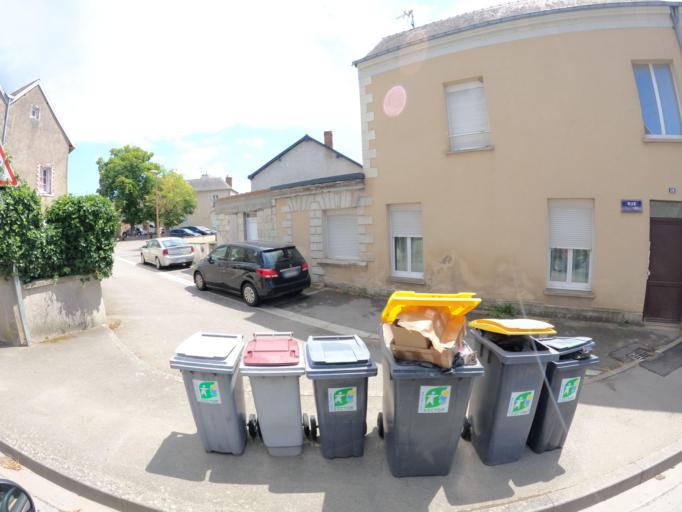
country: FR
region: Pays de la Loire
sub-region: Departement de Maine-et-Loire
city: Champigne
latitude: 47.6631
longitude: -0.5727
